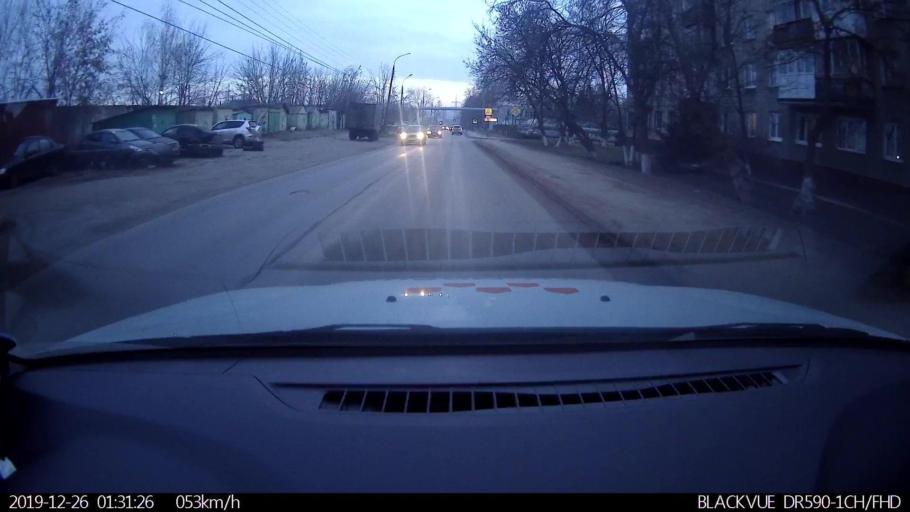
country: RU
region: Nizjnij Novgorod
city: Nizhniy Novgorod
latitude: 56.2676
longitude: 43.8989
